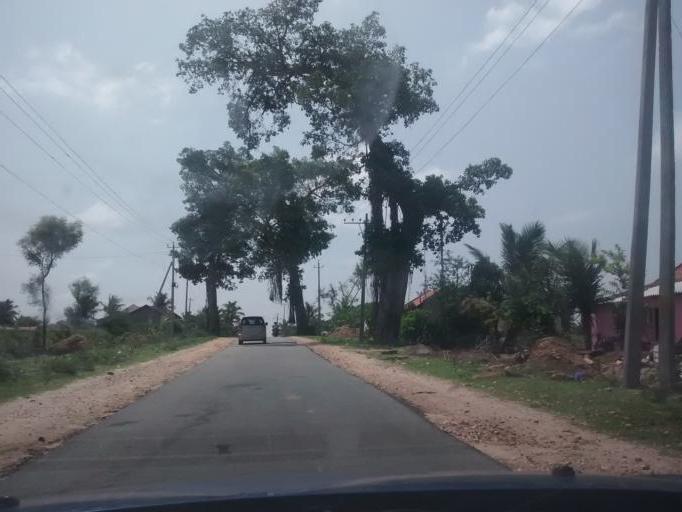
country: IN
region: Karnataka
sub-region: Mandya
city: Krishnarajpet
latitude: 12.5723
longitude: 76.3048
